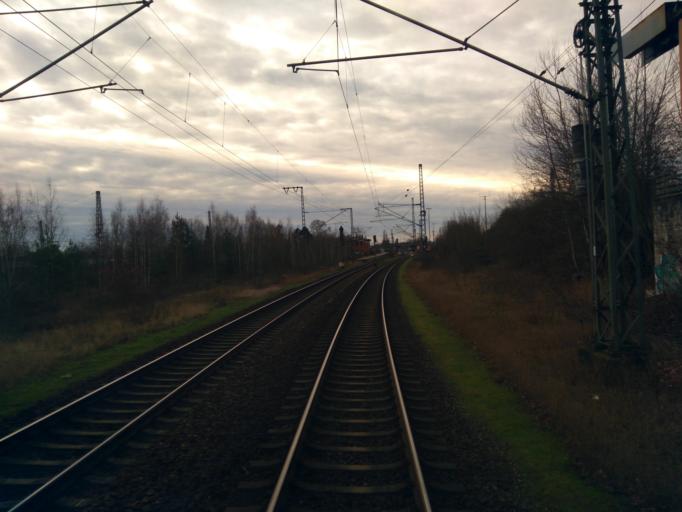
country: DE
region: Lower Saxony
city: Uelzen
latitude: 52.9729
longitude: 10.5551
